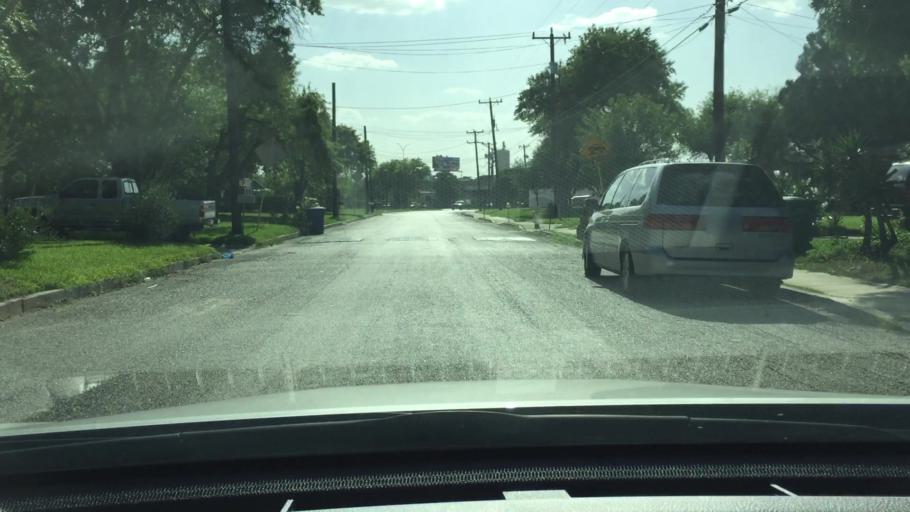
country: US
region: Texas
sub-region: Bexar County
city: Windcrest
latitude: 29.5327
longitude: -98.3869
